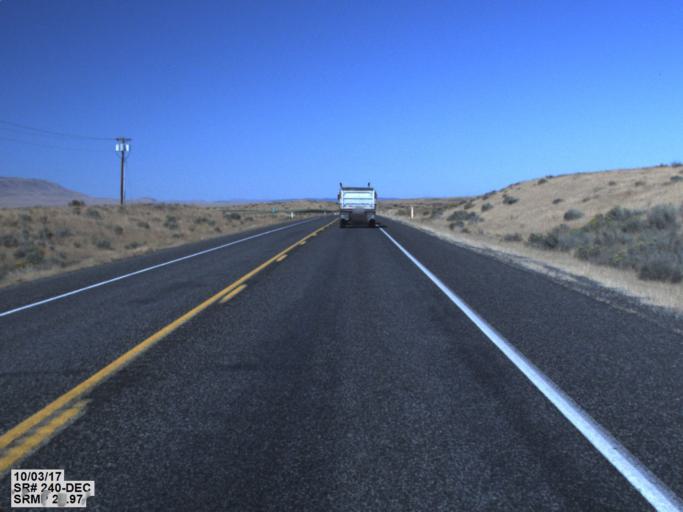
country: US
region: Washington
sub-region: Benton County
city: West Richland
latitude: 46.3429
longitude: -119.3488
